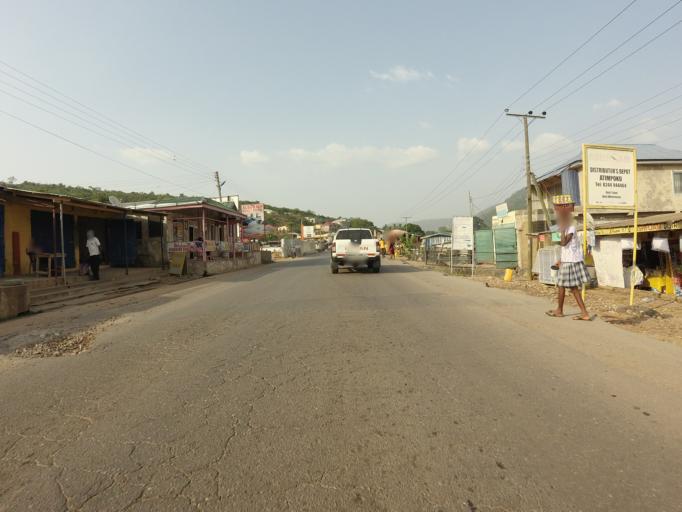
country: GH
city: Akropong
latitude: 6.2343
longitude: 0.0921
